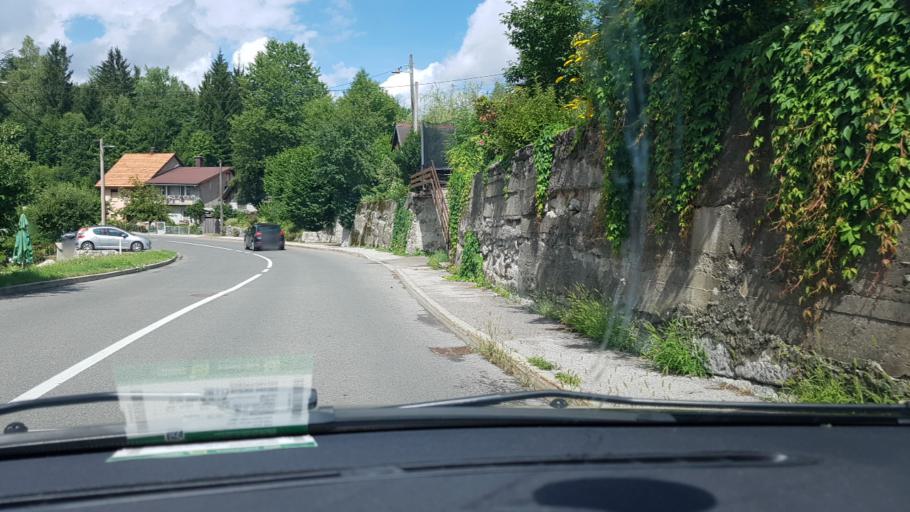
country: HR
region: Primorsko-Goranska
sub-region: Grad Delnice
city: Delnice
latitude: 45.3616
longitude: 14.7298
